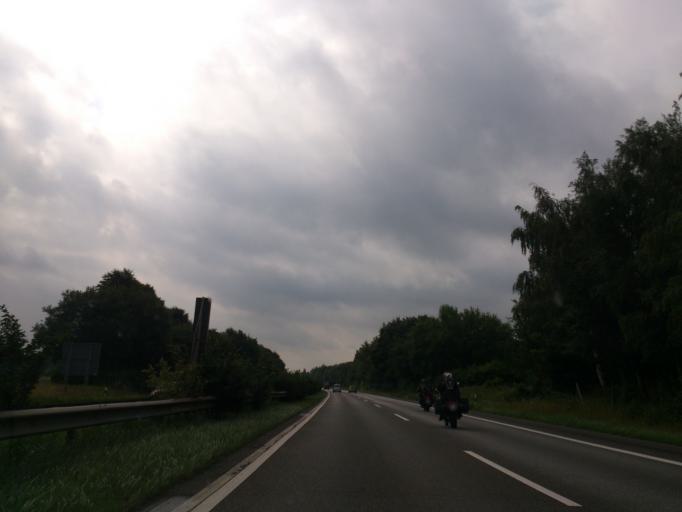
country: DE
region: Schleswig-Holstein
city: Seeth-Ekholt
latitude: 53.7354
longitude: 9.7190
